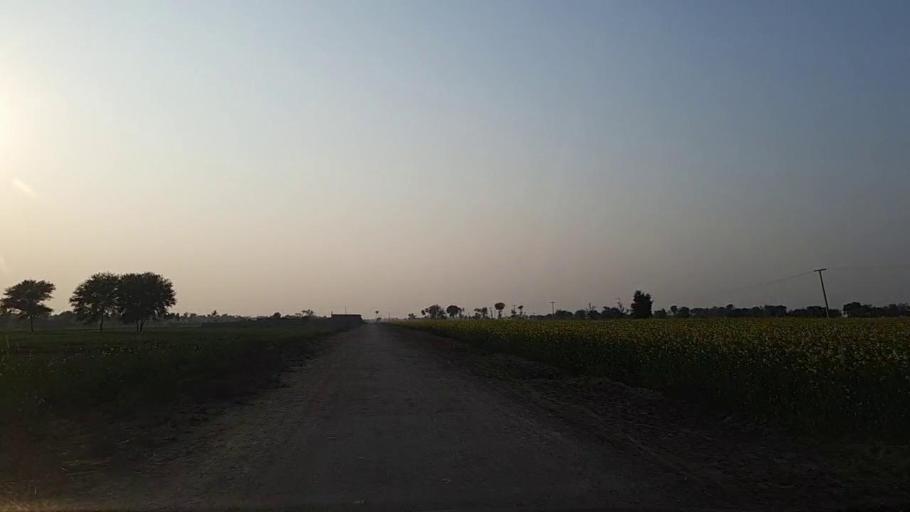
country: PK
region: Sindh
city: Daur
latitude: 26.4163
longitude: 68.3857
